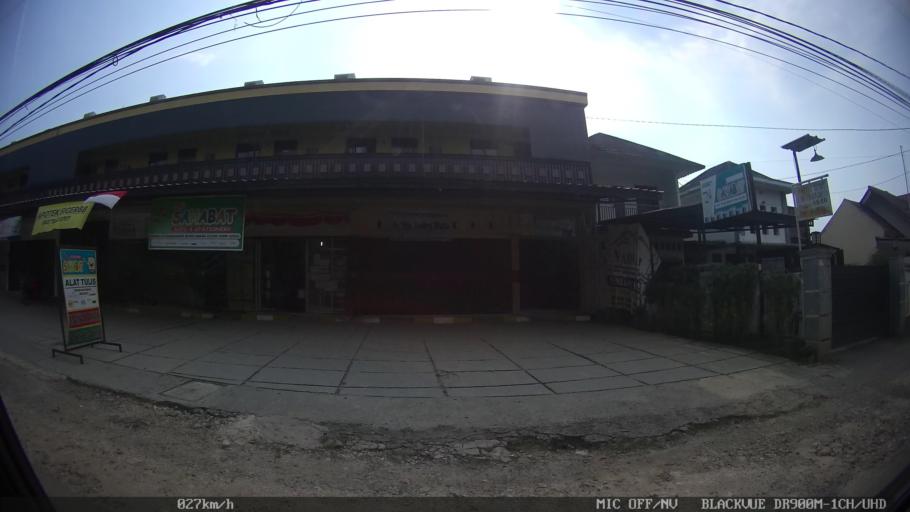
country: ID
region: Lampung
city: Kedaton
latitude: -5.3712
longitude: 105.2206
